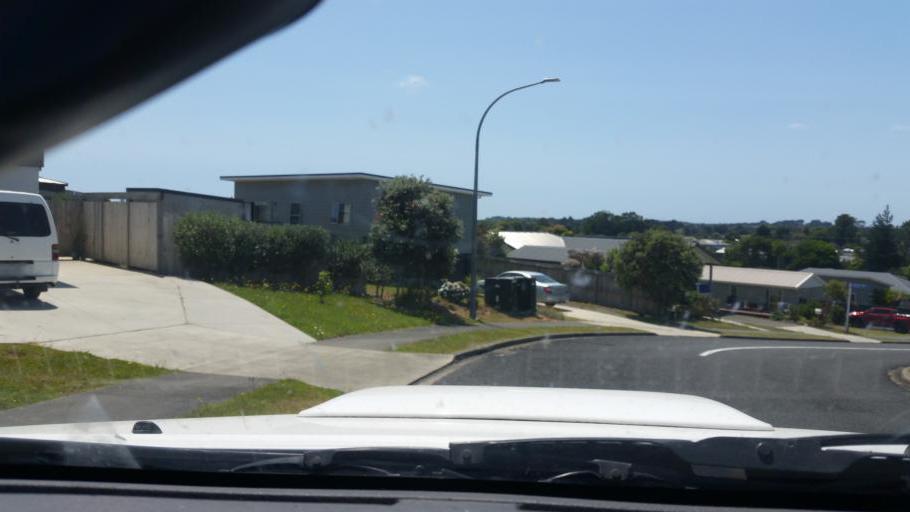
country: NZ
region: Auckland
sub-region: Auckland
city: Wellsford
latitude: -36.1243
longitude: 174.5721
